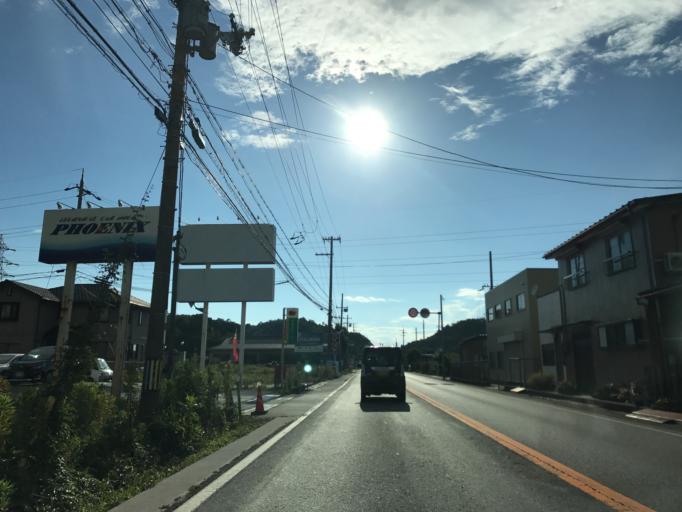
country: JP
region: Shiga Prefecture
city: Nagahama
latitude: 35.3257
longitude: 136.3100
